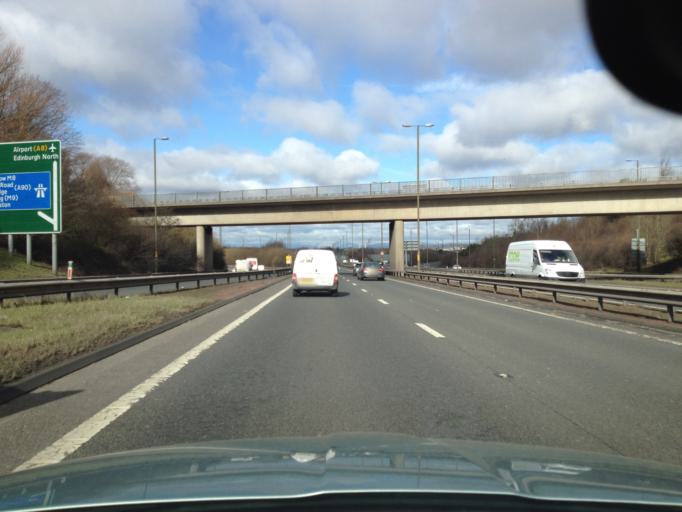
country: GB
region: Scotland
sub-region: Edinburgh
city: Currie
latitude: 55.9210
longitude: -3.3062
